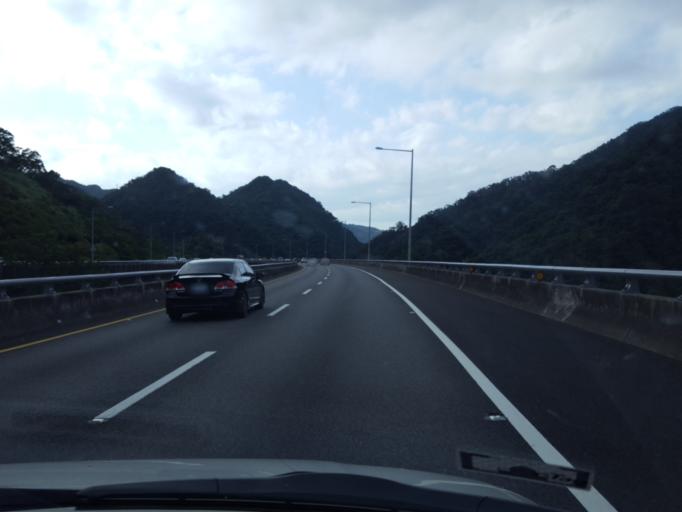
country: TW
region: Taipei
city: Taipei
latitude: 24.9801
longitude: 121.6746
